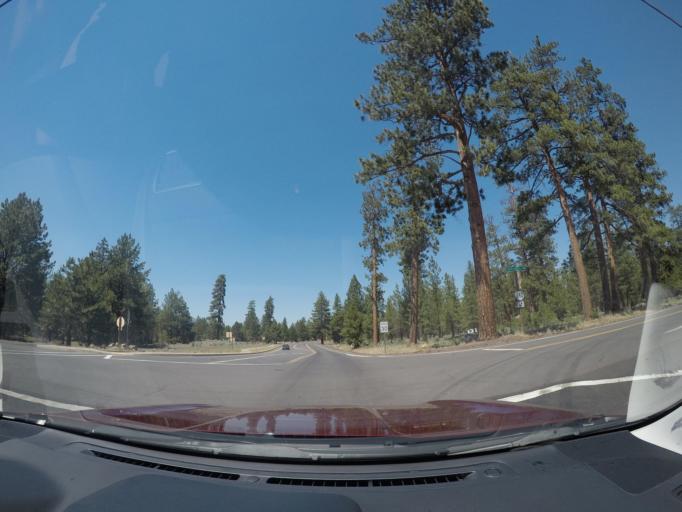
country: US
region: Oregon
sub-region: Deschutes County
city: Sisters
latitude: 44.2913
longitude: -121.5585
